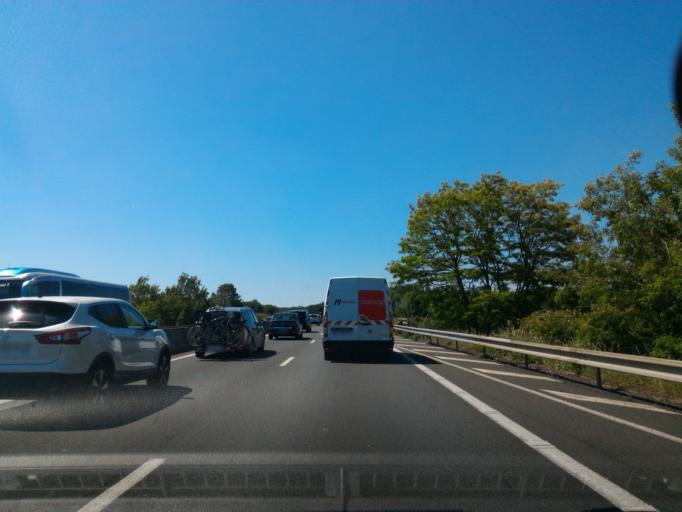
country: FR
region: Centre
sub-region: Departement d'Indre-et-Loire
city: Sorigny
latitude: 47.2399
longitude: 0.6606
